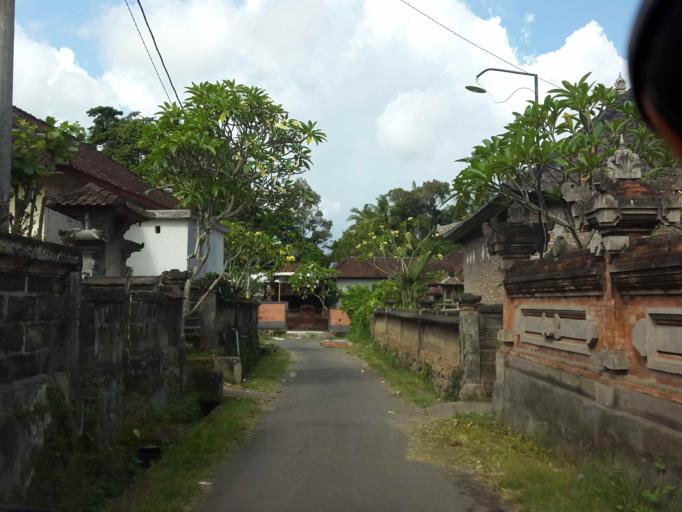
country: ID
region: Bali
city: Banjar Kelodan
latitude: -8.5186
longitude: 115.3669
